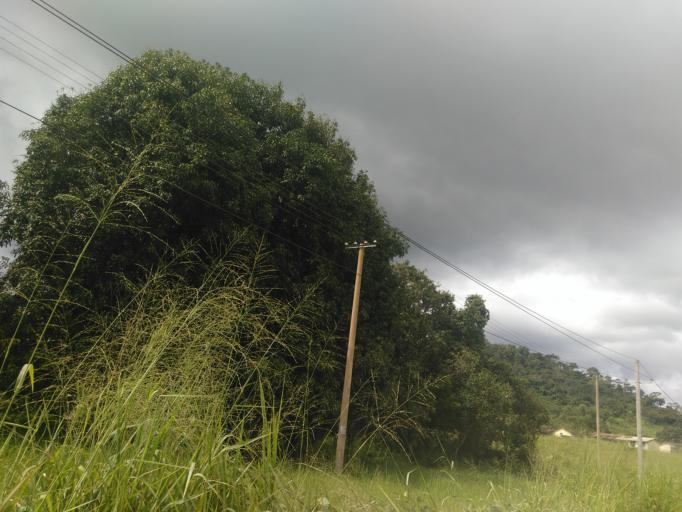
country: SL
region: Northern Province
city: Makali
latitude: 8.6291
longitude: -11.6602
